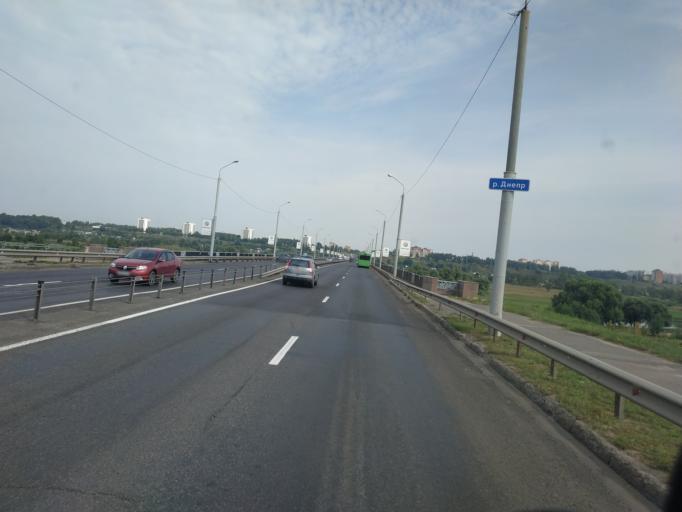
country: BY
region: Mogilev
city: Mahilyow
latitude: 53.8895
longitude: 30.3765
